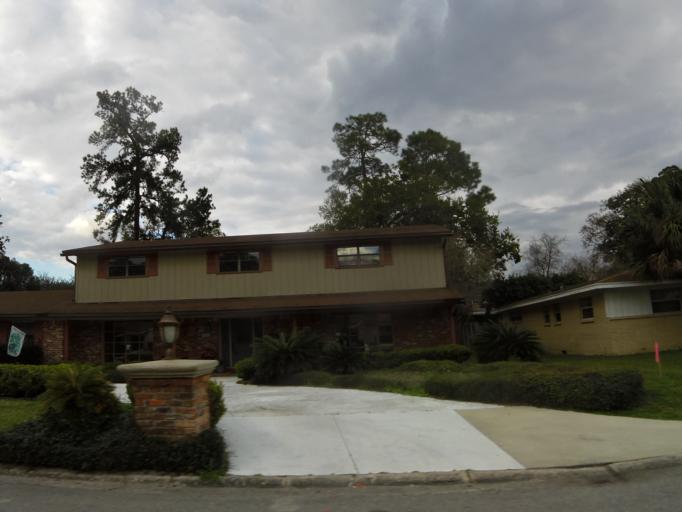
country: US
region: Florida
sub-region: Duval County
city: Jacksonville
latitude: 30.2502
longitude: -81.6349
